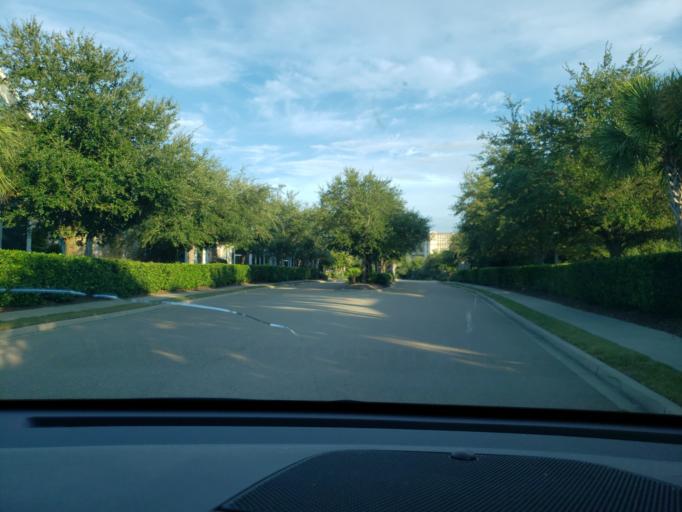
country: US
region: South Carolina
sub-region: Horry County
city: North Myrtle Beach
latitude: 33.7951
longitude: -78.7410
